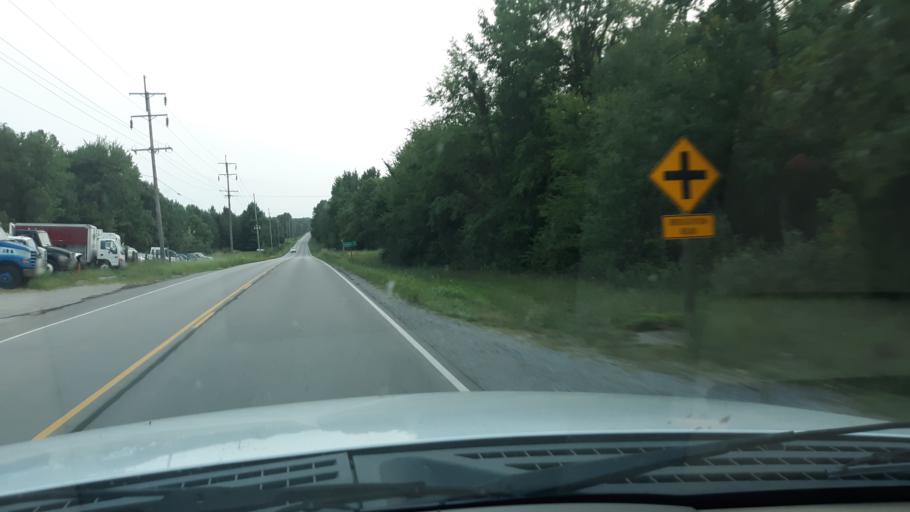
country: US
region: Illinois
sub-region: White County
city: Norris City
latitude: 37.9530
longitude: -88.3381
